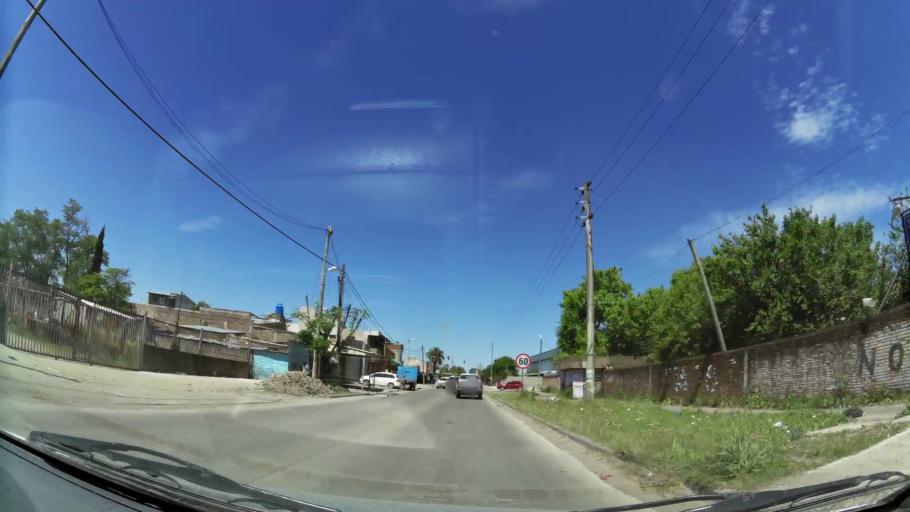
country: AR
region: Buenos Aires
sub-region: Partido de Lanus
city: Lanus
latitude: -34.7300
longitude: -58.3300
